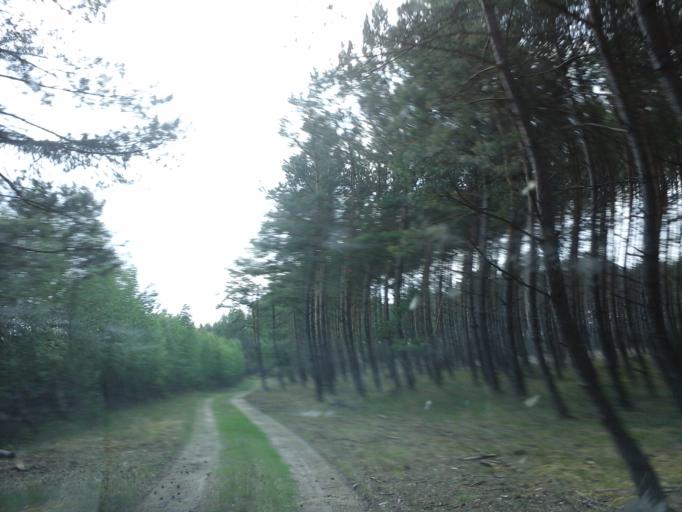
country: PL
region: West Pomeranian Voivodeship
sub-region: Powiat drawski
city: Kalisz Pomorski
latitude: 53.1813
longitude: 15.9378
